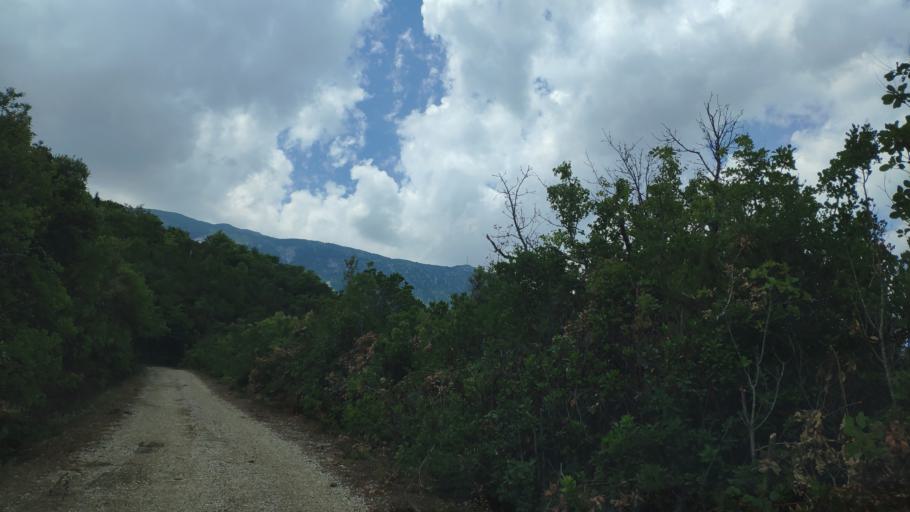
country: GR
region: Epirus
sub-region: Nomos Artas
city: Agios Dimitrios
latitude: 39.3141
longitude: 21.0186
